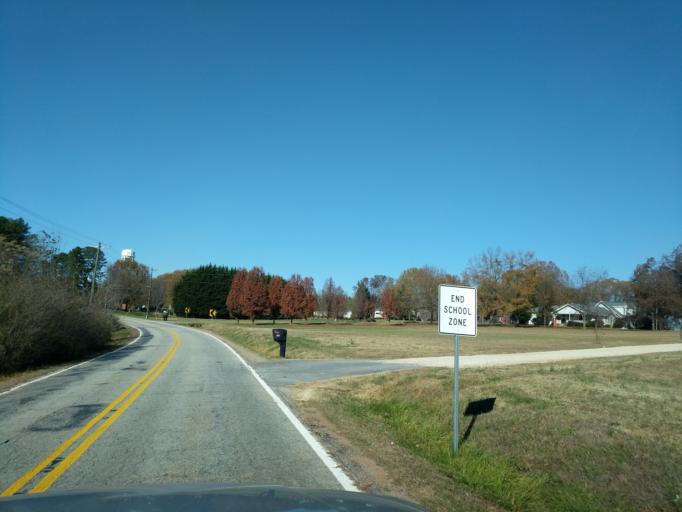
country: US
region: South Carolina
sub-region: Spartanburg County
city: Duncan
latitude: 34.9811
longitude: -82.1640
